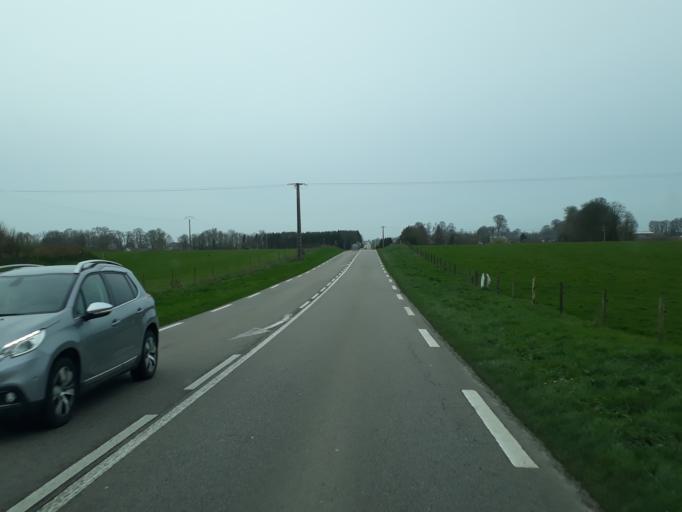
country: FR
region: Haute-Normandie
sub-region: Departement de la Seine-Maritime
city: Breaute
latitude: 49.6302
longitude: 0.3935
